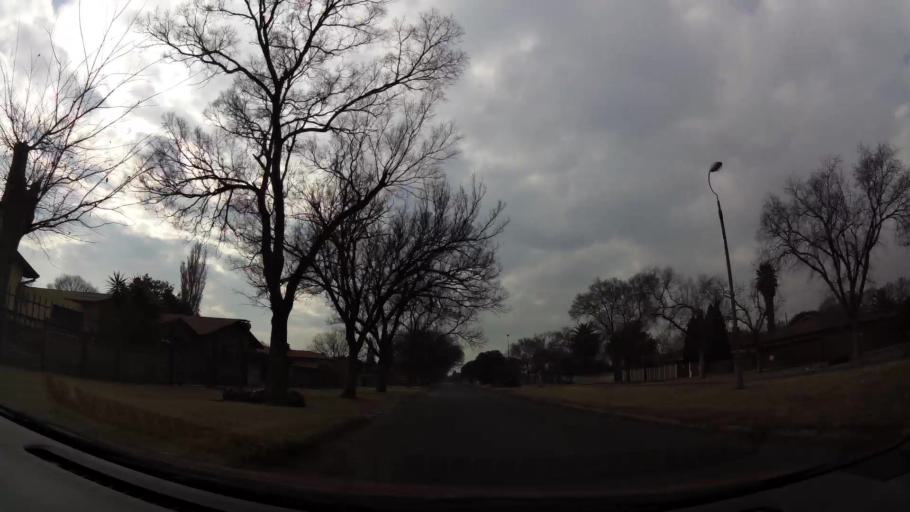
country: ZA
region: Gauteng
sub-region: Sedibeng District Municipality
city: Vanderbijlpark
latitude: -26.6844
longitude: 27.8308
